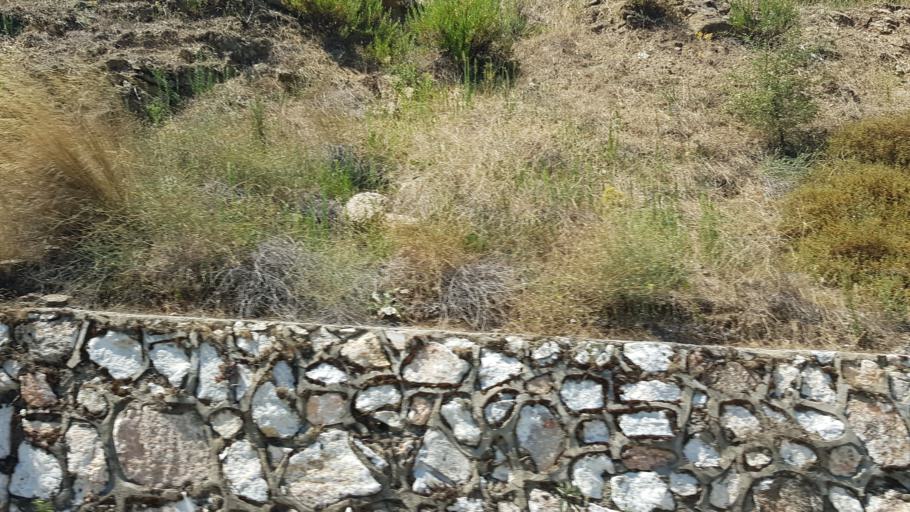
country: TR
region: Aydin
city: Akcaova
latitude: 37.5096
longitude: 28.1010
